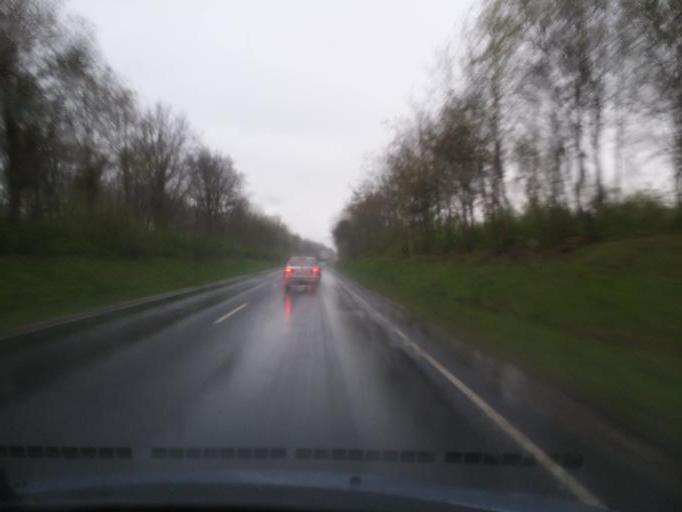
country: DK
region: South Denmark
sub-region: Odense Kommune
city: Bellinge
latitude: 55.3509
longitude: 10.3334
